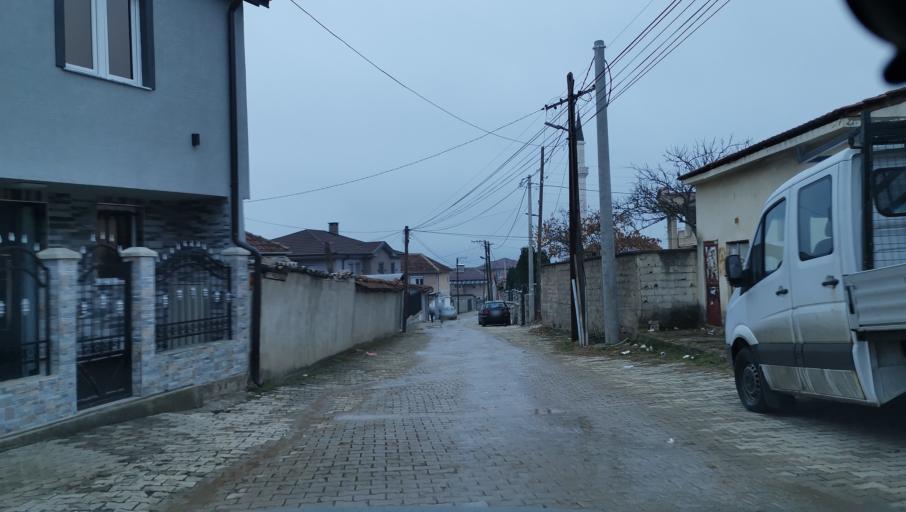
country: MK
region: Debar
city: Debar
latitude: 41.5275
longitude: 20.5248
